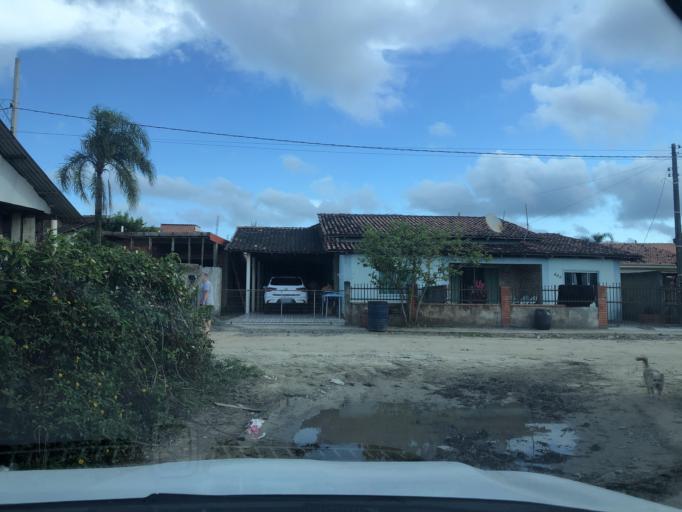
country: BR
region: Santa Catarina
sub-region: Sao Francisco Do Sul
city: Sao Francisco do Sul
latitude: -26.2259
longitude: -48.5232
